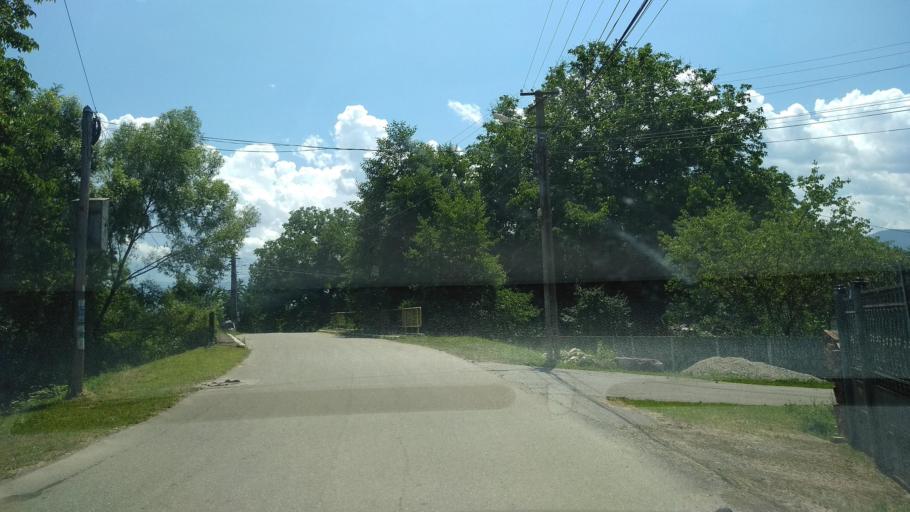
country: RO
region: Hunedoara
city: Densus
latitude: 45.5541
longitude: 22.8226
